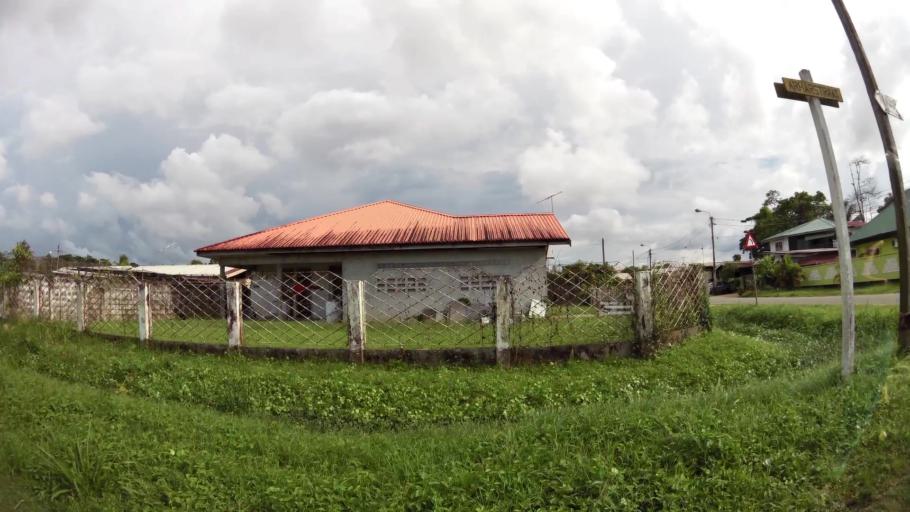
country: SR
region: Paramaribo
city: Paramaribo
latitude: 5.8561
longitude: -55.1794
